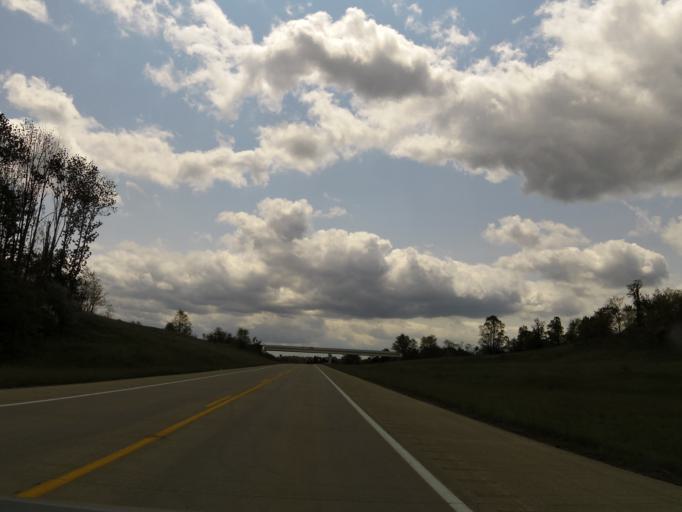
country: US
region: Ohio
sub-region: Athens County
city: Athens
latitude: 39.2591
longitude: -82.0829
